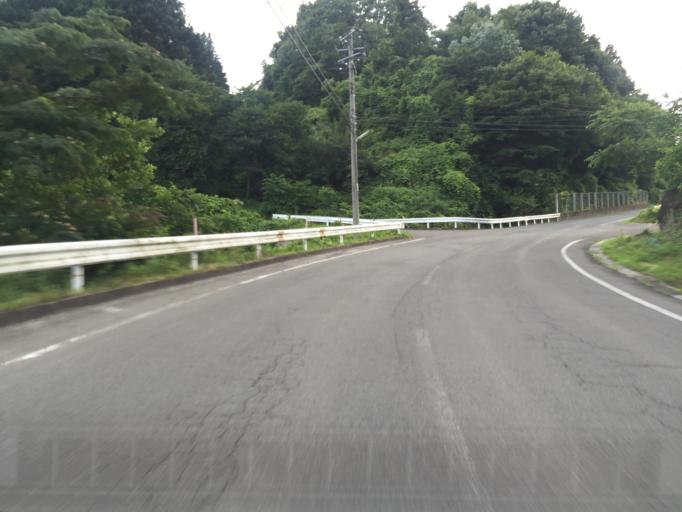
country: JP
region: Fukushima
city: Hobaramachi
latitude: 37.7017
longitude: 140.5809
